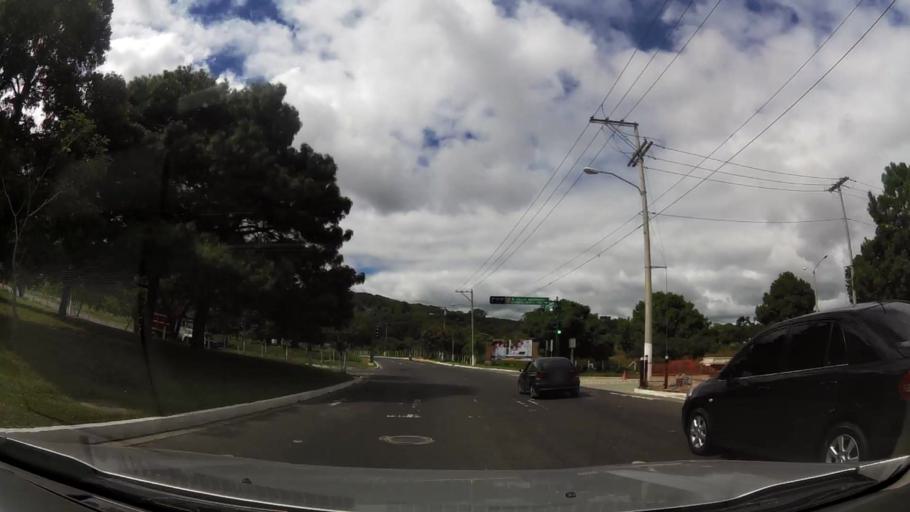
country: GT
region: Guatemala
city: Guatemala City
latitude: 14.6554
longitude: -90.5420
